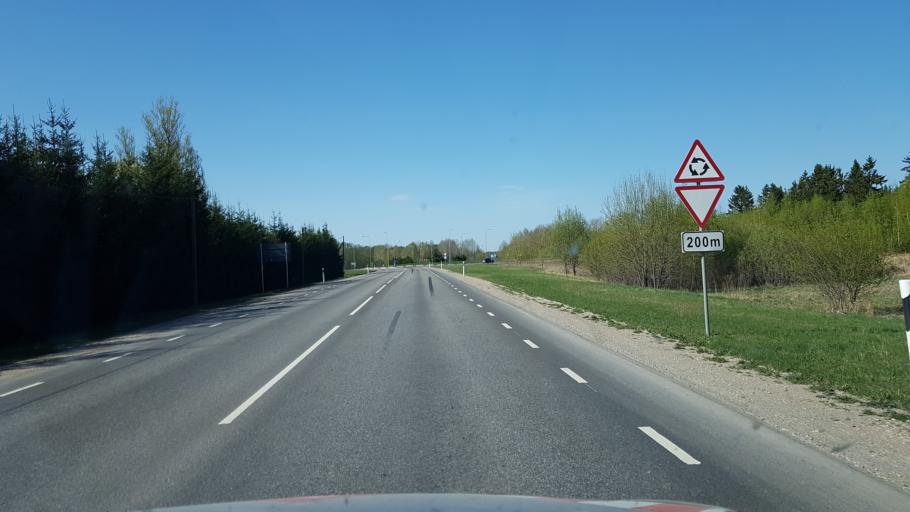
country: EE
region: Viljandimaa
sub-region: Viljandi linn
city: Viljandi
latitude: 58.3536
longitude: 25.5602
